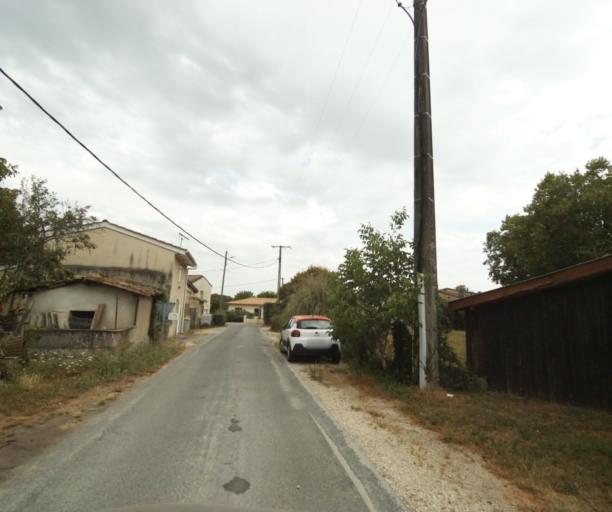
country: FR
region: Aquitaine
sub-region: Departement de la Gironde
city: La Sauve
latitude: 44.7582
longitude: -0.3297
